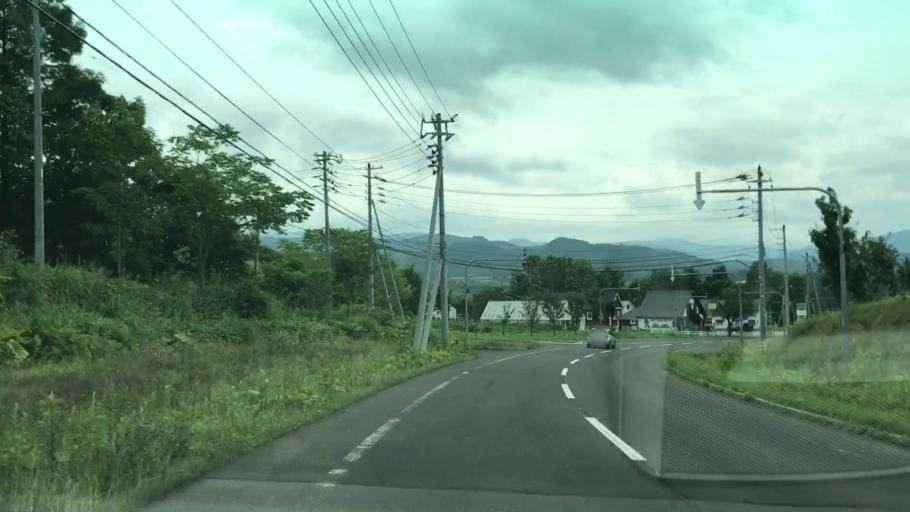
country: JP
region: Hokkaido
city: Yoichi
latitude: 43.1078
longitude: 140.8228
